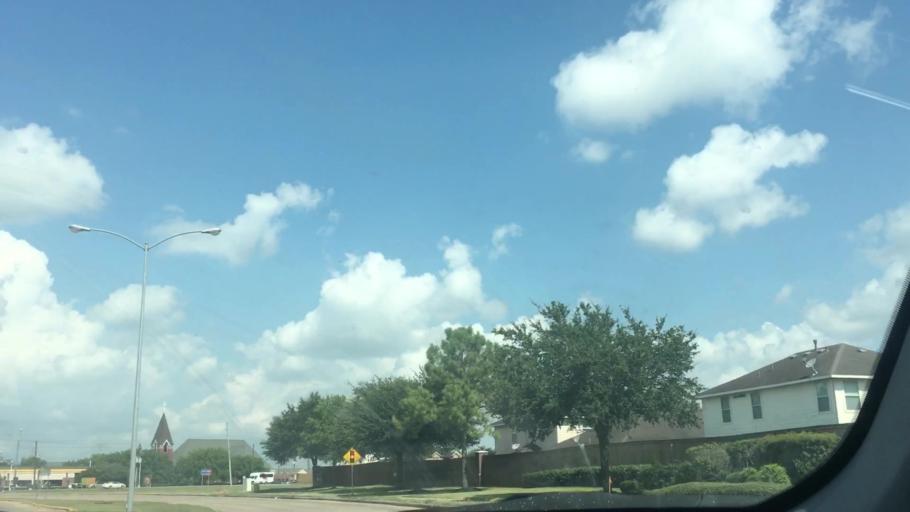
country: US
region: Texas
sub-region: Fort Bend County
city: Fifth Street
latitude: 29.6003
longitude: -95.5624
